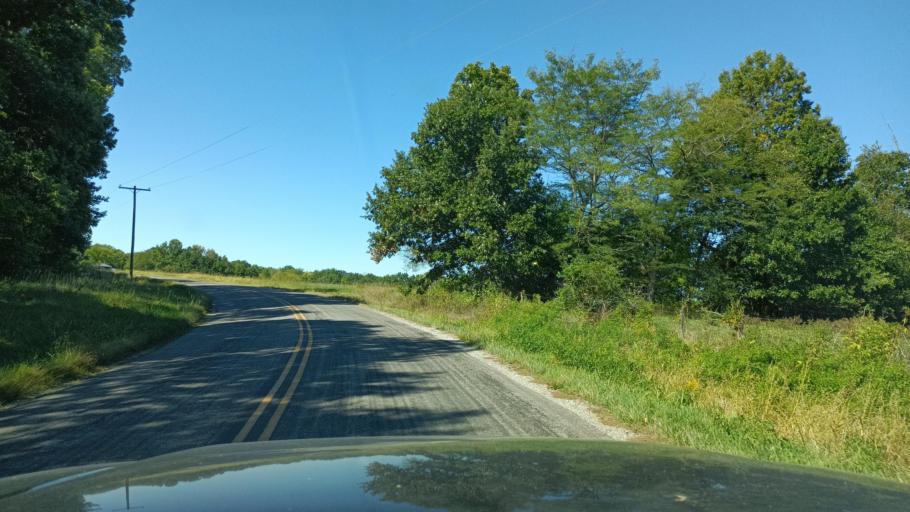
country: US
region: Missouri
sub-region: Scotland County
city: Memphis
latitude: 40.3563
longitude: -92.2593
